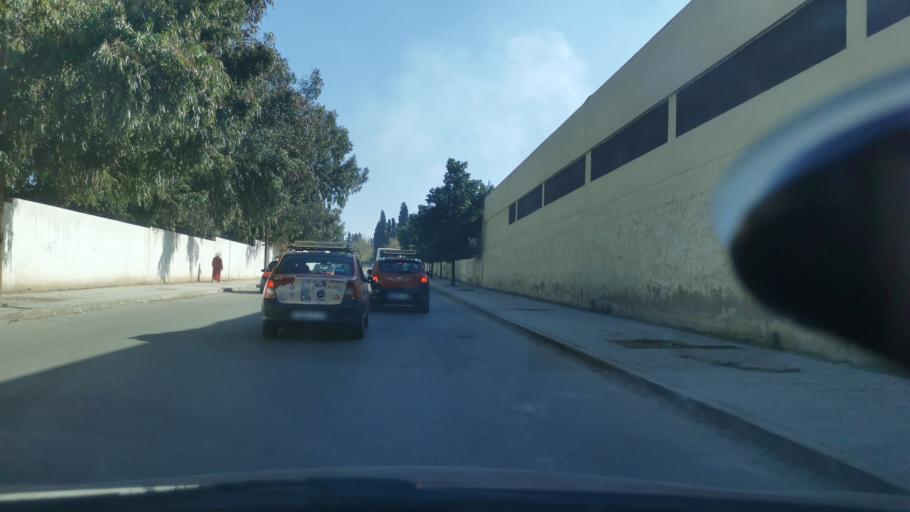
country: MA
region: Fes-Boulemane
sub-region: Fes
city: Fes
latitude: 34.0329
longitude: -4.9890
